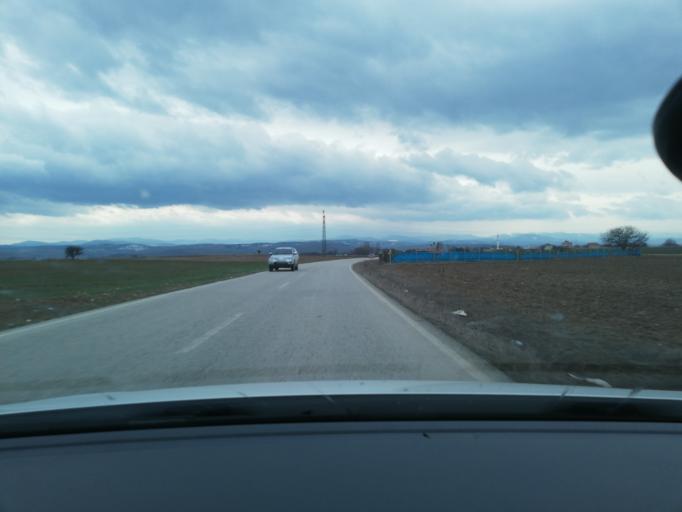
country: TR
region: Bolu
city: Gerede
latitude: 40.7658
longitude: 32.2007
